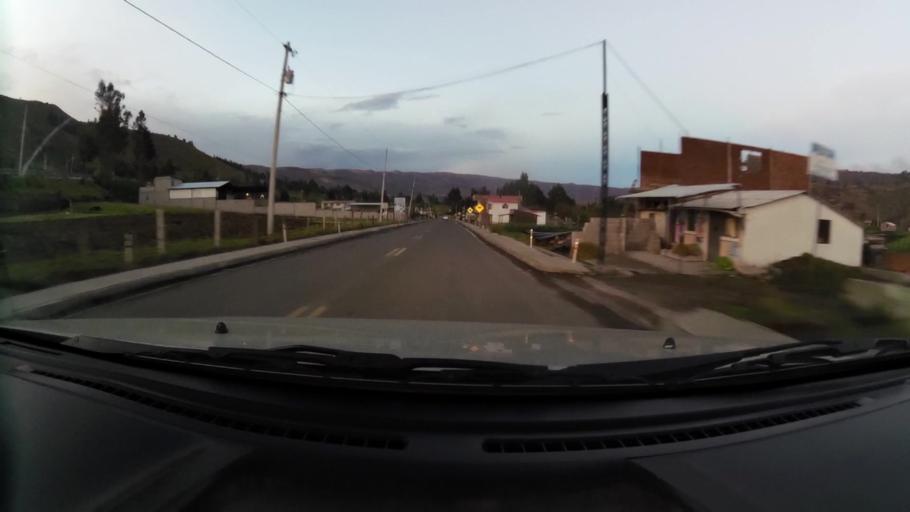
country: EC
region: Chimborazo
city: Riobamba
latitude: -1.9204
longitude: -78.7005
